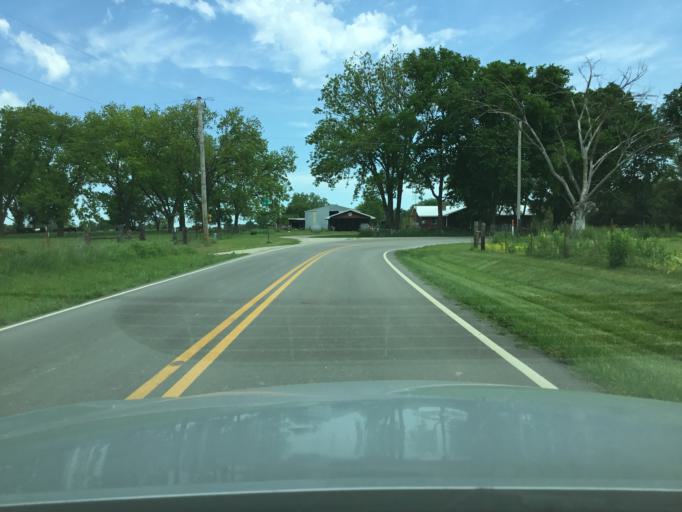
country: US
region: Kansas
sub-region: Montgomery County
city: Coffeyville
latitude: 37.0074
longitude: -95.5904
